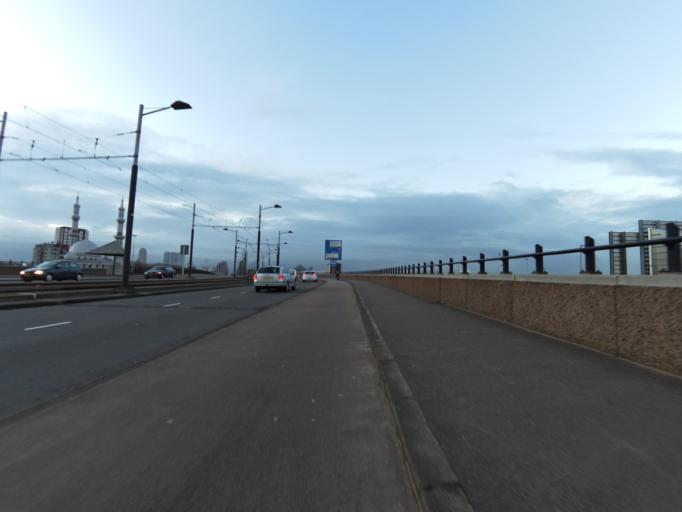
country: NL
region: South Holland
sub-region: Gemeente Rotterdam
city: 's-Gravenland
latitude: 51.8983
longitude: 4.5165
